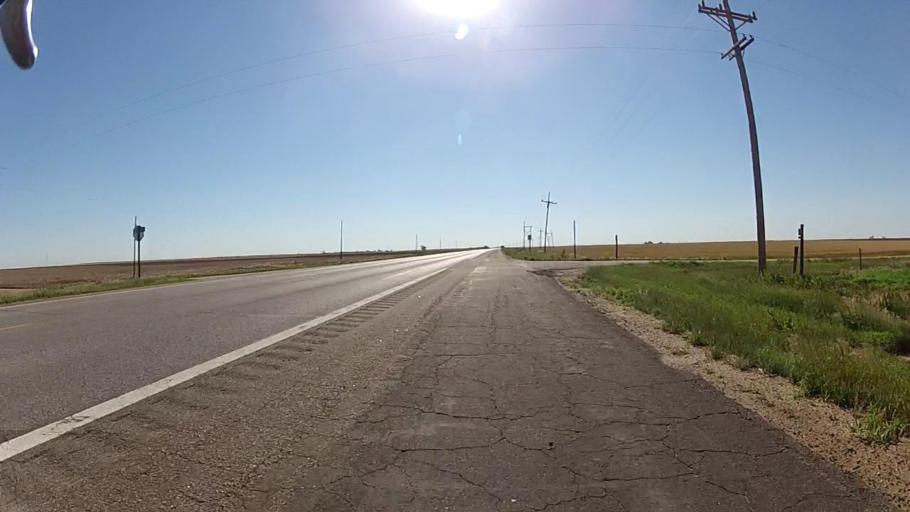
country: US
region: Kansas
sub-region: Kiowa County
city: Greensburg
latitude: 37.5863
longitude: -99.6673
